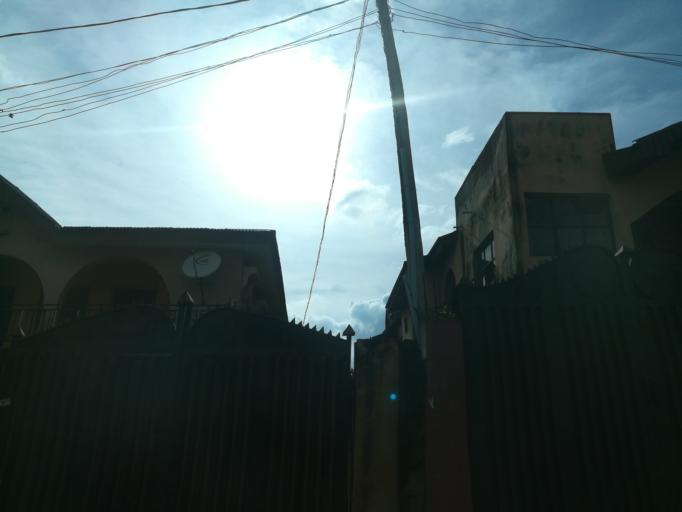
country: NG
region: Lagos
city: Ikorodu
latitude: 6.5986
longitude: 3.5055
